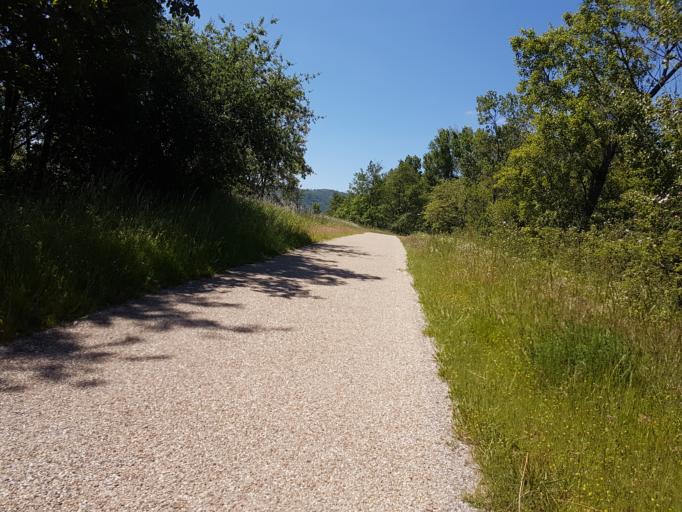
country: FR
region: Rhone-Alpes
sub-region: Departement de la Drome
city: Saint-Vallier
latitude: 45.1425
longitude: 4.8141
